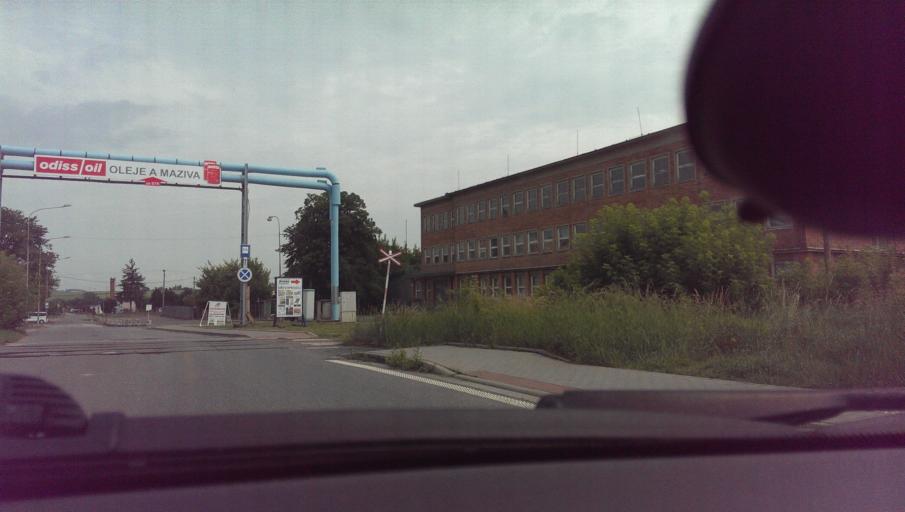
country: CZ
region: Zlin
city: Tecovice
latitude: 49.2071
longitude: 17.5797
